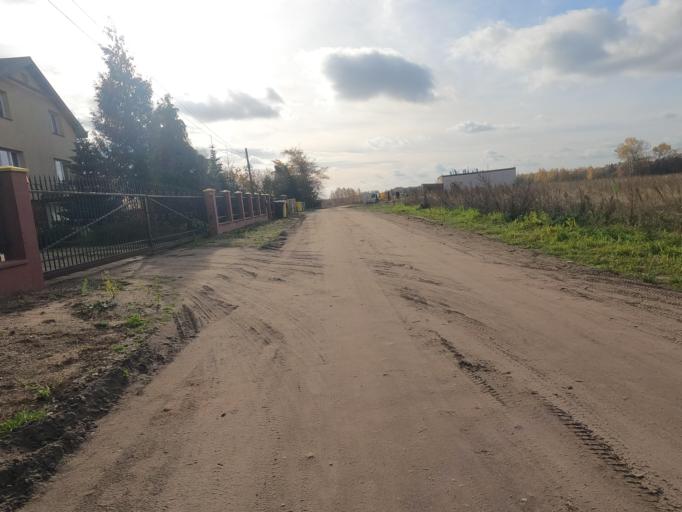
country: PL
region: Pomeranian Voivodeship
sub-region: Powiat starogardzki
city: Starogard Gdanski
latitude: 53.9769
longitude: 18.4845
